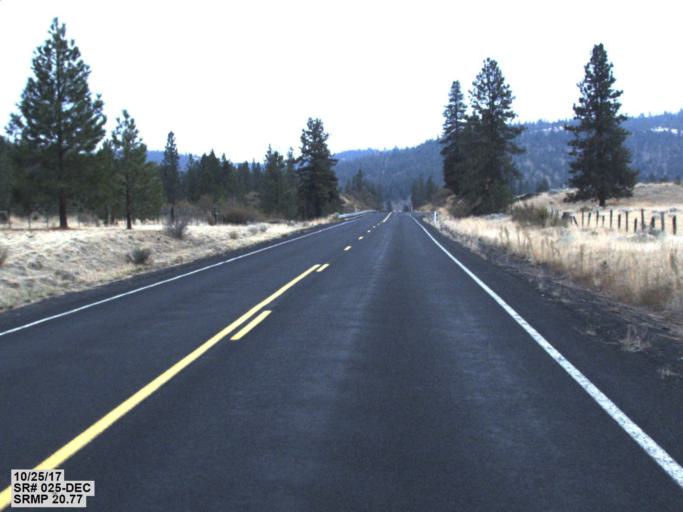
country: US
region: Washington
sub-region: Lincoln County
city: Davenport
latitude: 47.9049
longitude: -118.2750
